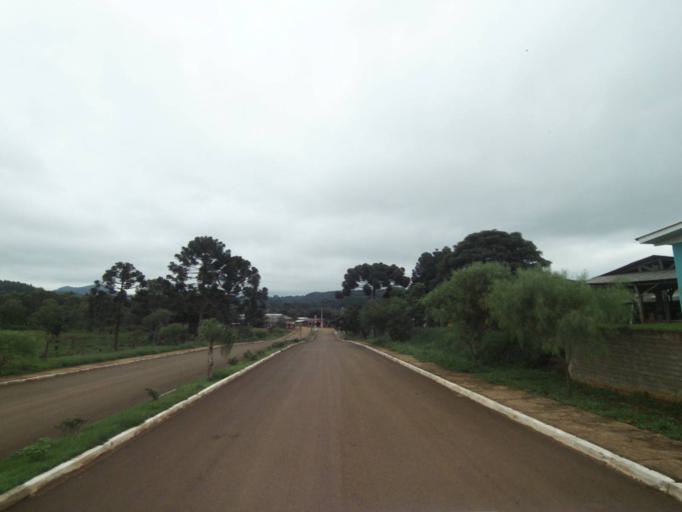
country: BR
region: Parana
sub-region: Pitanga
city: Pitanga
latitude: -24.9362
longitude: -51.8721
